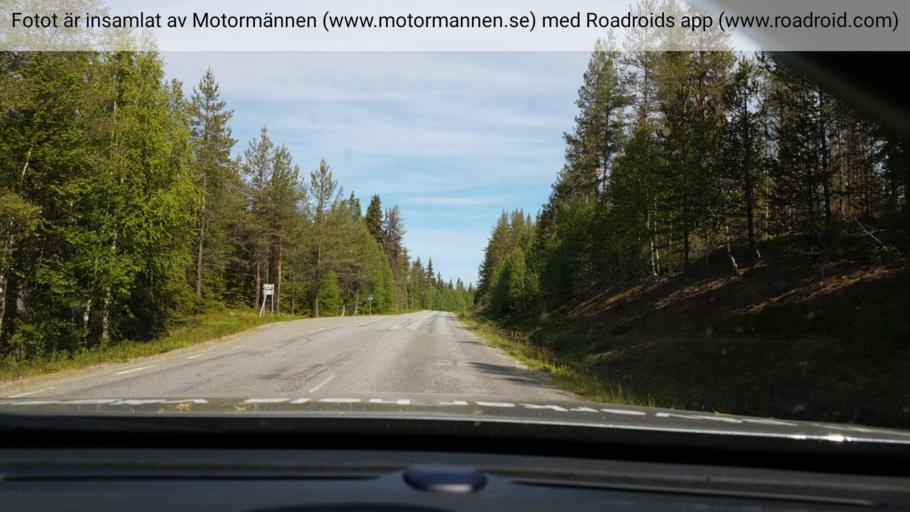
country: SE
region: Vaesterbotten
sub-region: Vilhelmina Kommun
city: Sjoberg
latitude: 64.5882
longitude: 15.8700
